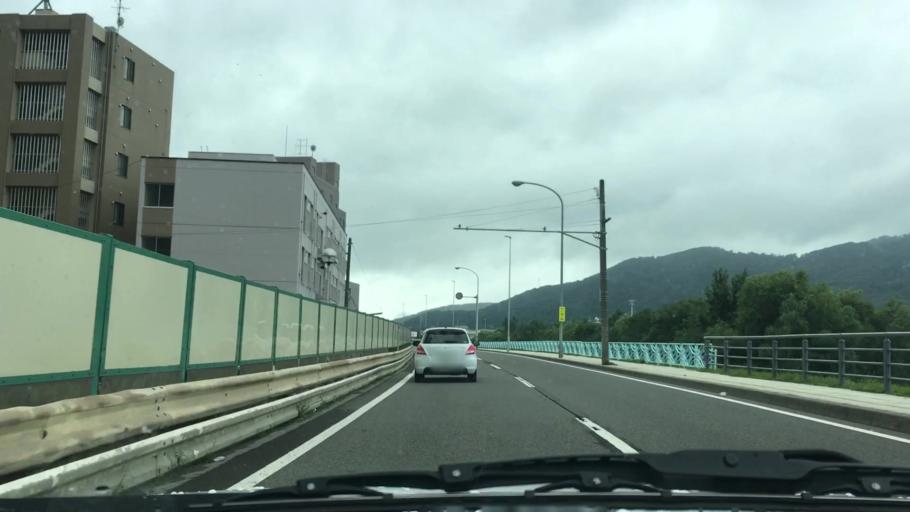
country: JP
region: Hokkaido
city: Sapporo
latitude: 43.0384
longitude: 141.3583
